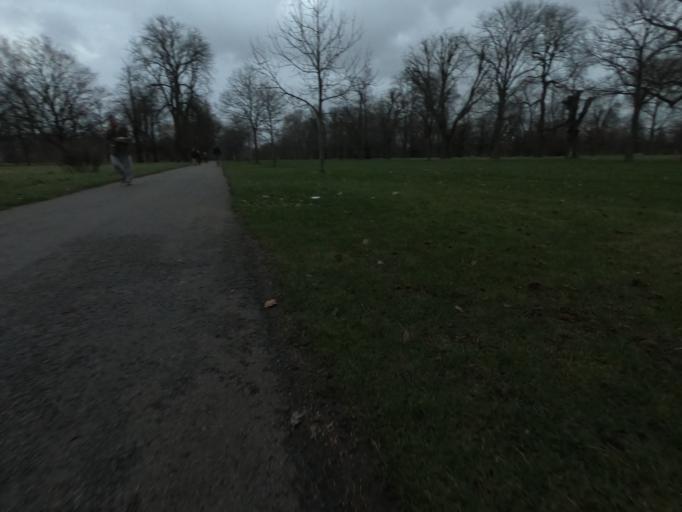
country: GB
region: England
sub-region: Greater London
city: Bayswater
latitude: 51.5075
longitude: -0.1823
